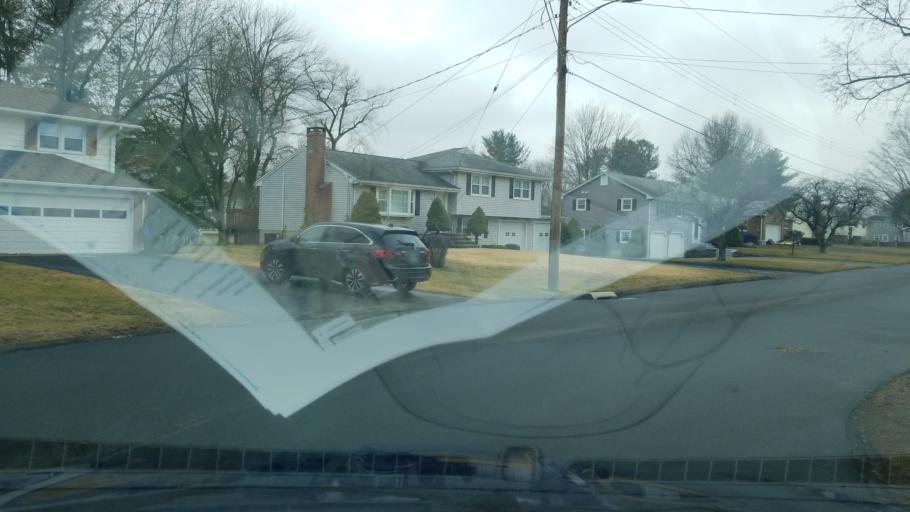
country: US
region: Connecticut
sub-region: Hartford County
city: Wethersfield
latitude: 41.6727
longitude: -72.6694
